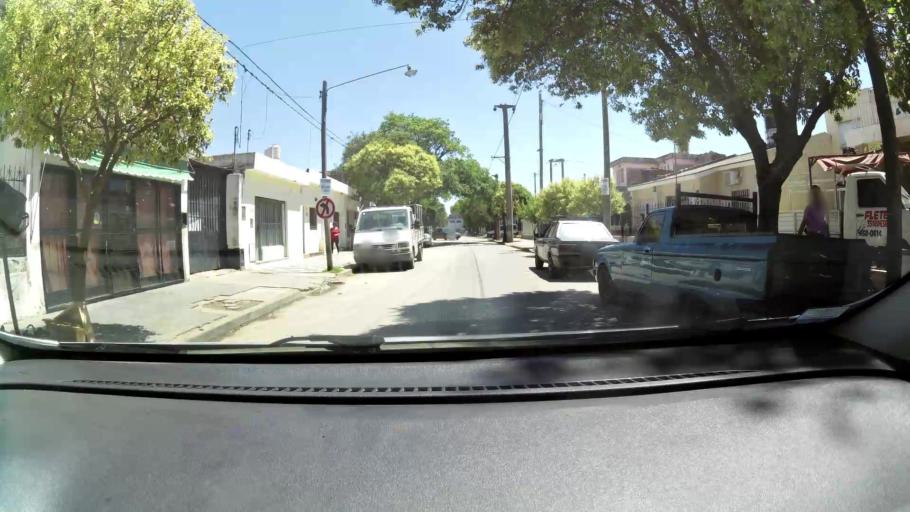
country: AR
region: Cordoba
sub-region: Departamento de Capital
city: Cordoba
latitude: -31.4347
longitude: -64.1272
